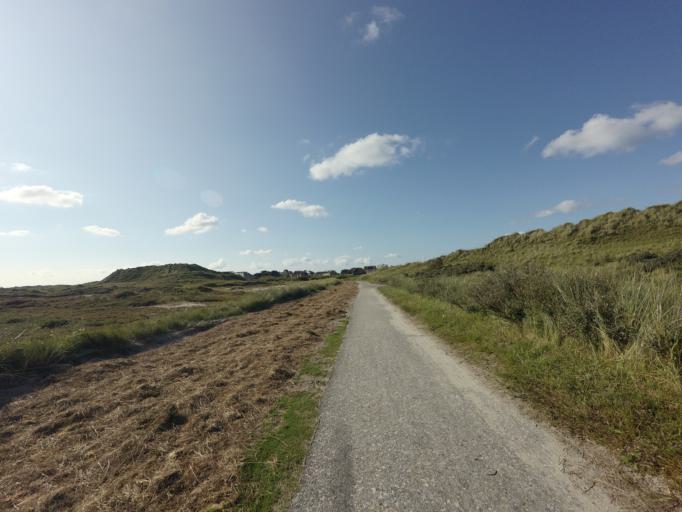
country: NL
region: Friesland
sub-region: Gemeente Terschelling
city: West-Terschelling
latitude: 53.3971
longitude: 5.2619
